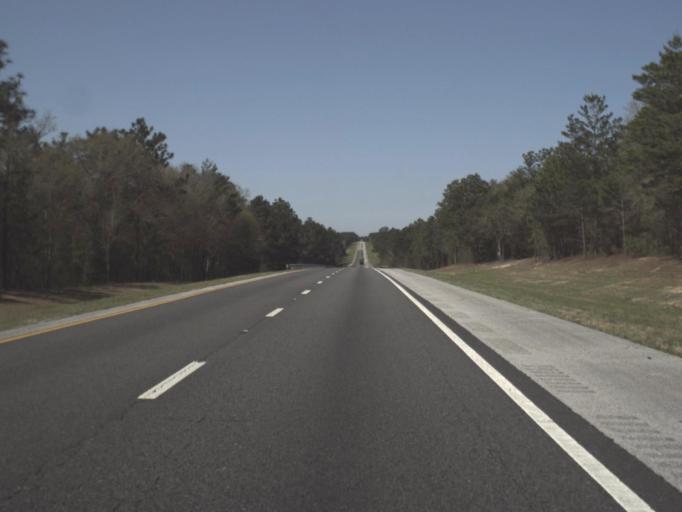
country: US
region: Florida
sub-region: Okaloosa County
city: Crestview
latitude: 30.7326
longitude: -86.3804
